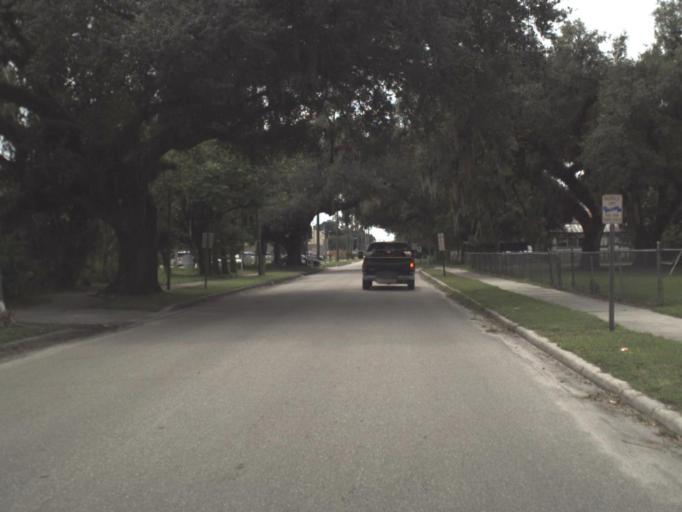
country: US
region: Florida
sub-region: Hendry County
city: LaBelle
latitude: 26.7659
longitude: -81.4385
